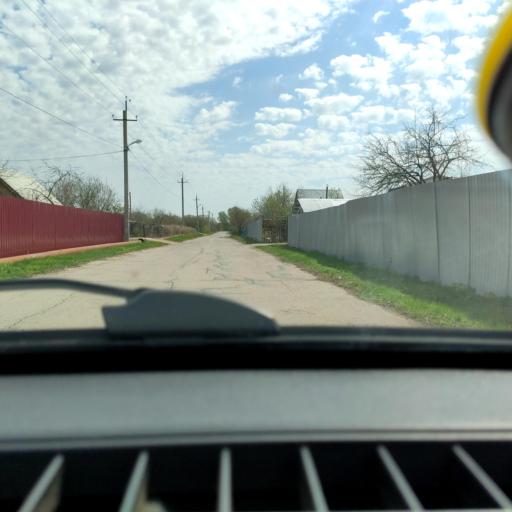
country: RU
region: Samara
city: Tol'yatti
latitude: 53.6990
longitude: 49.4467
